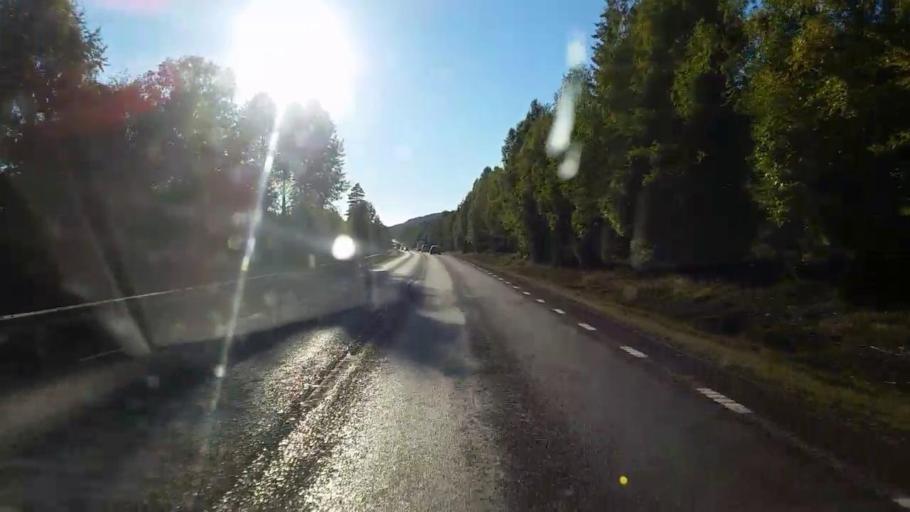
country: SE
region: Gaevleborg
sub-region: Hudiksvalls Kommun
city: Delsbo
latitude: 61.8066
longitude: 16.4059
